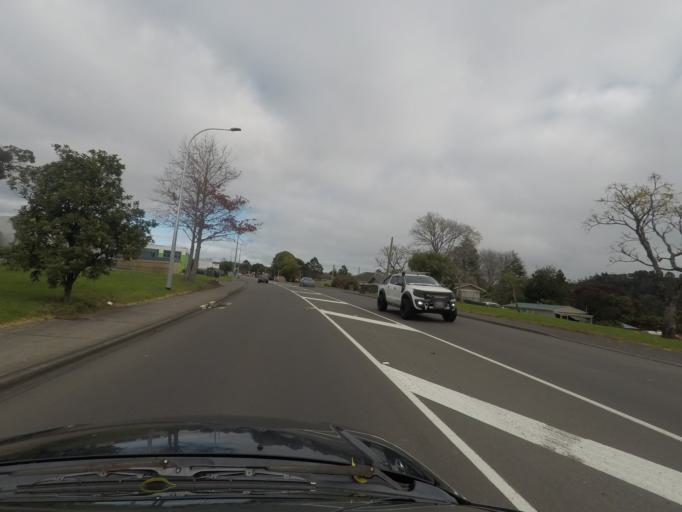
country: NZ
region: Auckland
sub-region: Auckland
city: Rosebank
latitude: -36.8637
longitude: 174.5896
